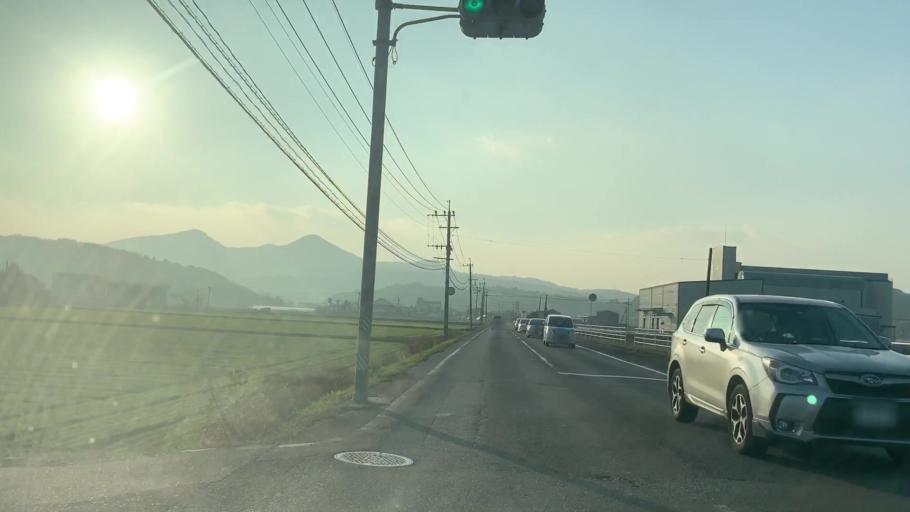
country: JP
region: Saga Prefecture
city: Saga-shi
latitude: 33.2732
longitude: 130.1940
